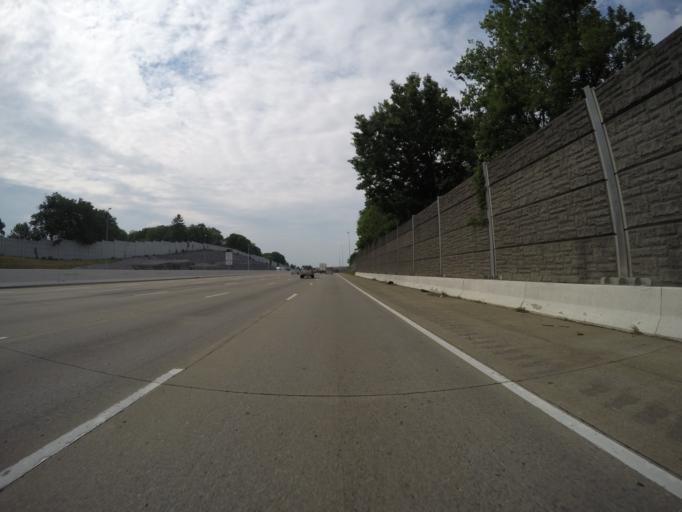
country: US
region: Tennessee
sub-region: Davidson County
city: Goodlettsville
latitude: 36.2600
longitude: -86.7386
